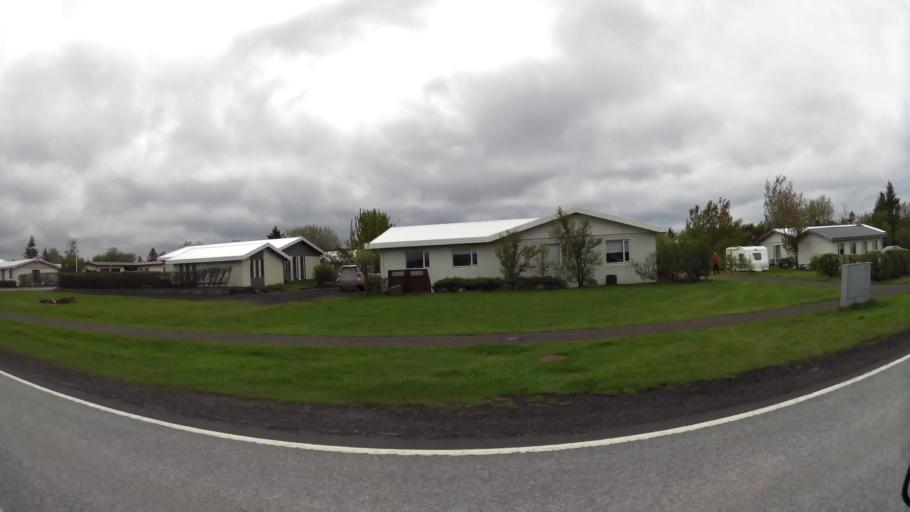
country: IS
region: Capital Region
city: Alftanes
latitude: 64.1092
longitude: -22.0126
